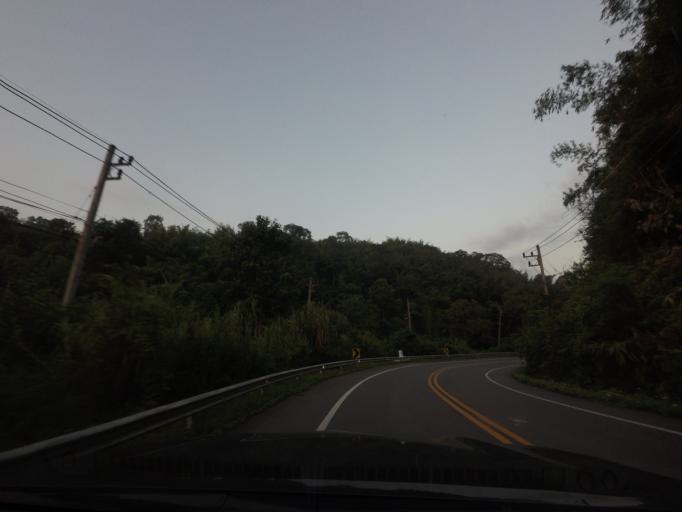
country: TH
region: Nan
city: Na Noi
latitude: 18.4308
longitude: 100.6992
